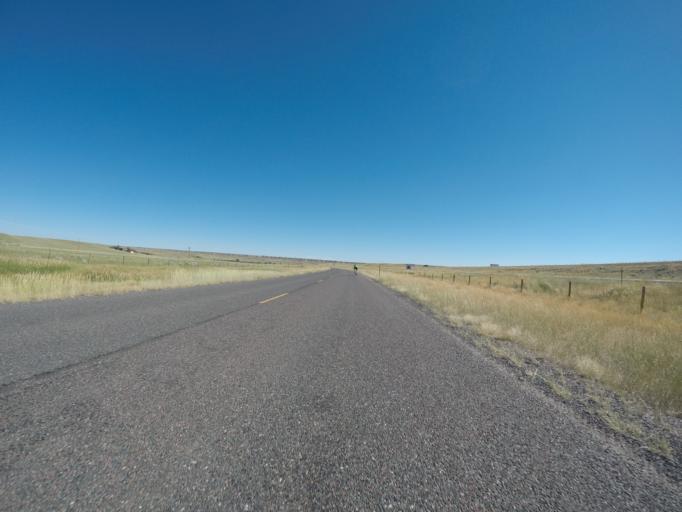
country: US
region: Wyoming
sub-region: Platte County
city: Wheatland
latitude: 41.7311
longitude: -104.8301
